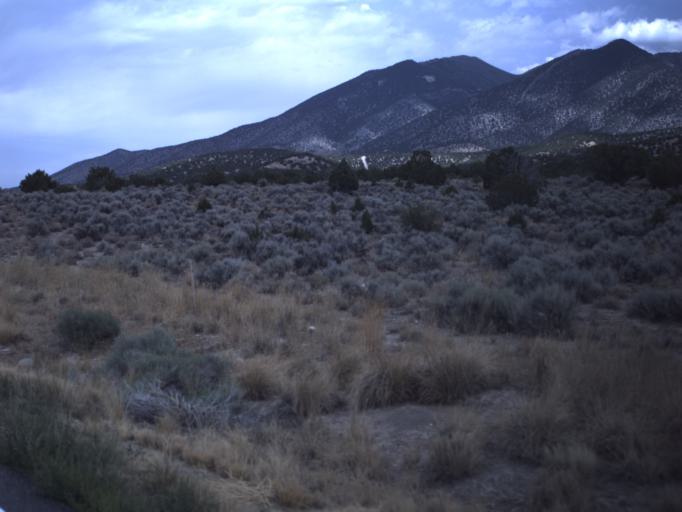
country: US
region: Utah
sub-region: Tooele County
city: Tooele
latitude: 40.3355
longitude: -112.2990
